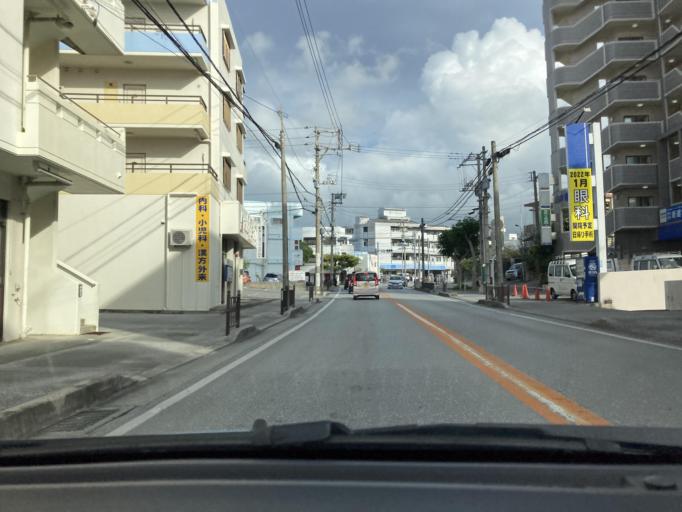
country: JP
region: Okinawa
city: Tomigusuku
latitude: 26.1856
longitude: 127.6597
